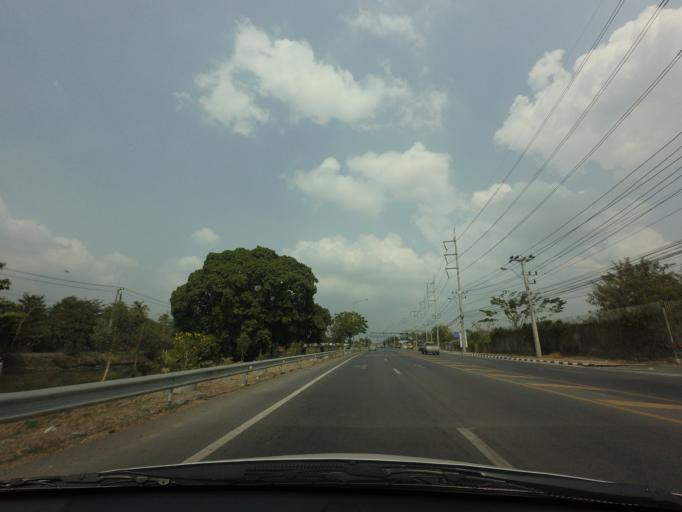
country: TH
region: Pathum Thani
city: Thanyaburi
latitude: 14.0576
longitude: 100.7101
